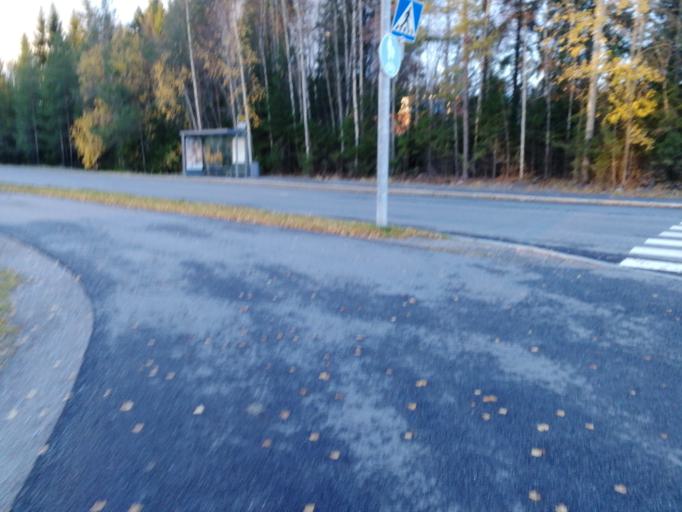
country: FI
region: Pirkanmaa
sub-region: Tampere
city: Tampere
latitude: 61.4529
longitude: 23.9010
